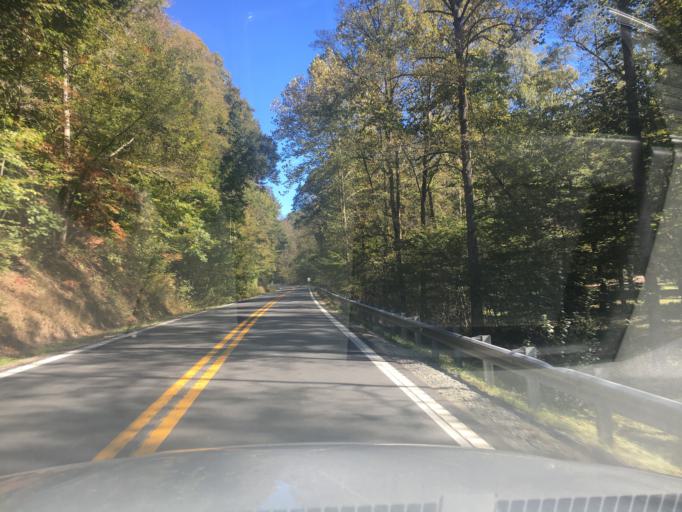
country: US
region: North Carolina
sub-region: Burke County
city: Glen Alpine
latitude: 35.5752
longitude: -81.8441
